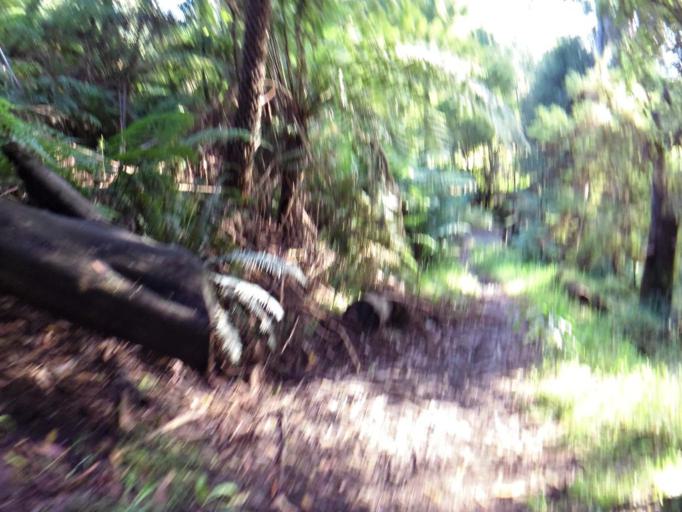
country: AU
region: Victoria
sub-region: Cardinia
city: Emerald
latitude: -37.9218
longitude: 145.4332
